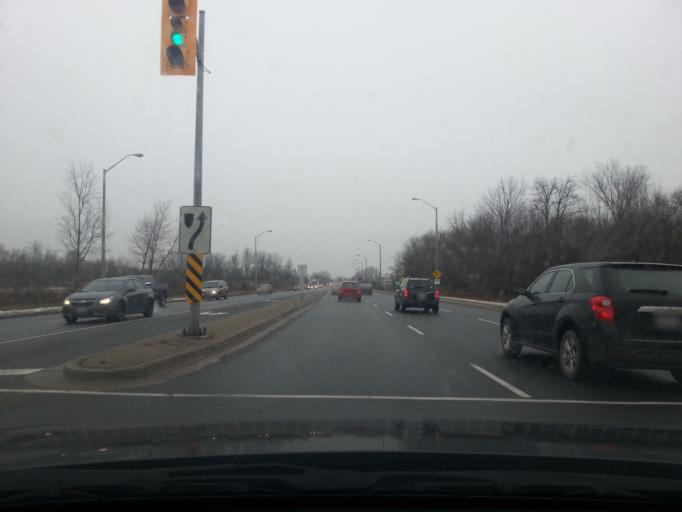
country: CA
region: Ontario
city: Peterborough
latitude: 44.2696
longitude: -78.3452
